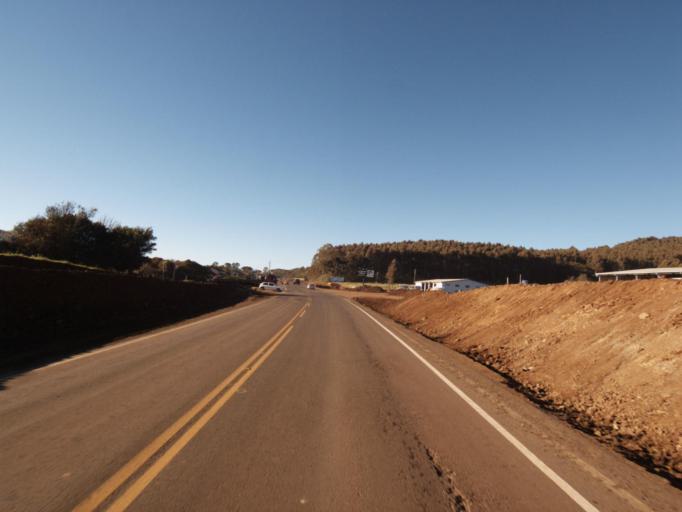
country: AR
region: Misiones
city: Bernardo de Irigoyen
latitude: -26.4605
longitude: -53.5094
